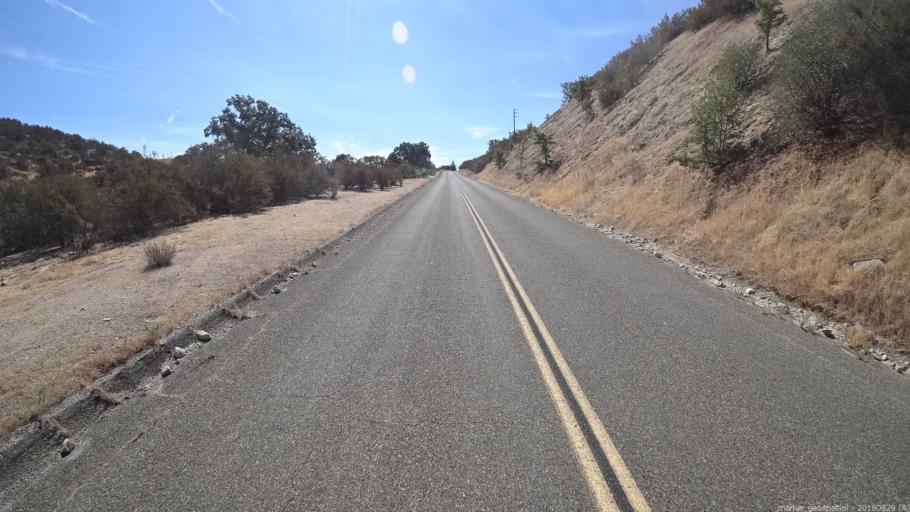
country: US
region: California
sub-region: San Luis Obispo County
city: Lake Nacimiento
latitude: 35.8068
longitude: -120.9807
